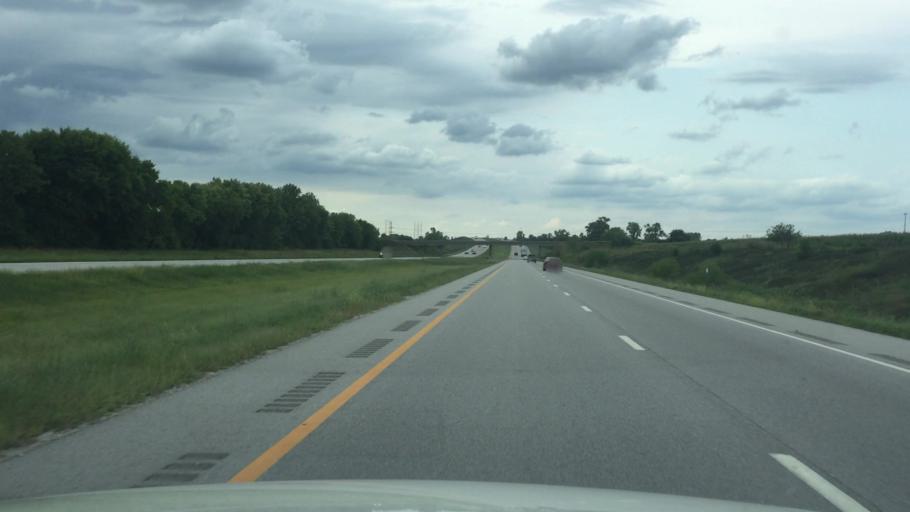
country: US
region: Kansas
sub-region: Miami County
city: Louisburg
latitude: 38.7347
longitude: -94.6763
